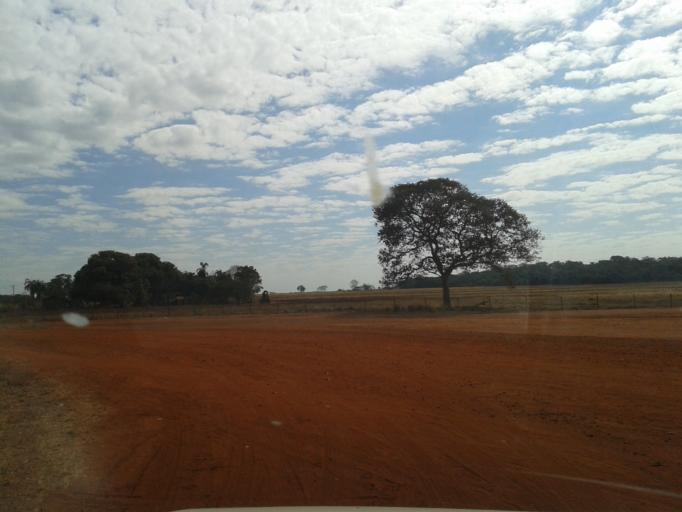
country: BR
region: Minas Gerais
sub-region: Ituiutaba
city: Ituiutaba
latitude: -18.9190
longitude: -49.4452
